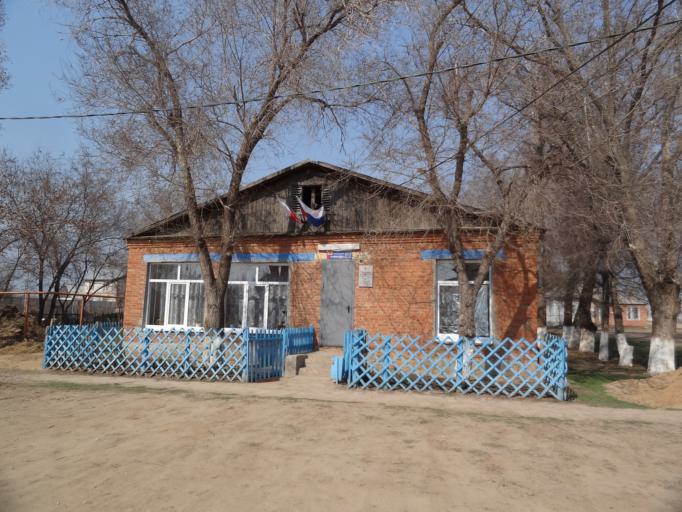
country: RU
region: Saratov
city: Privolzhskiy
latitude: 51.3041
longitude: 45.9592
